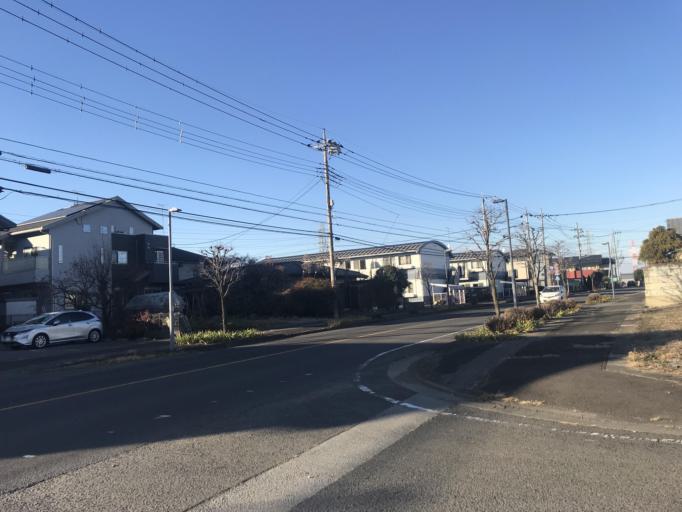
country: JP
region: Tochigi
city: Kaminokawa
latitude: 36.4373
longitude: 139.8710
